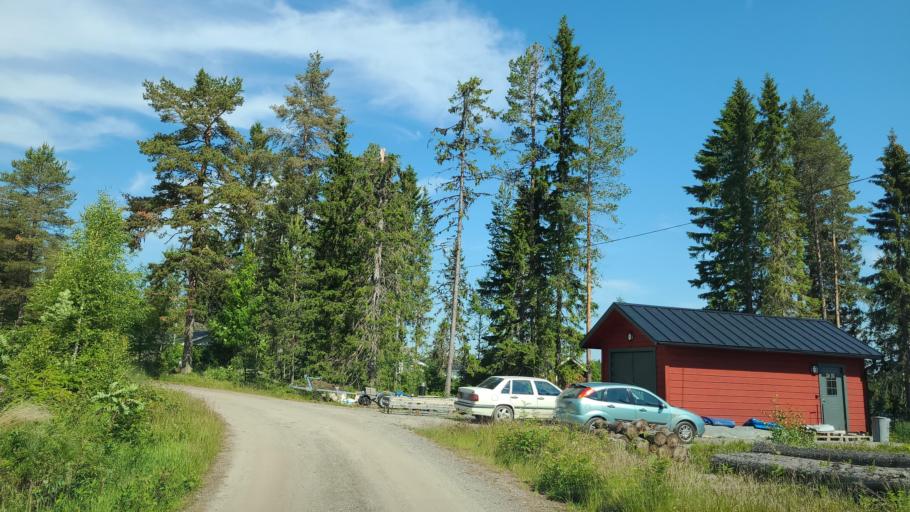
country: SE
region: Vaesterbotten
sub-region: Robertsfors Kommun
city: Robertsfors
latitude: 64.1389
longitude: 20.9632
